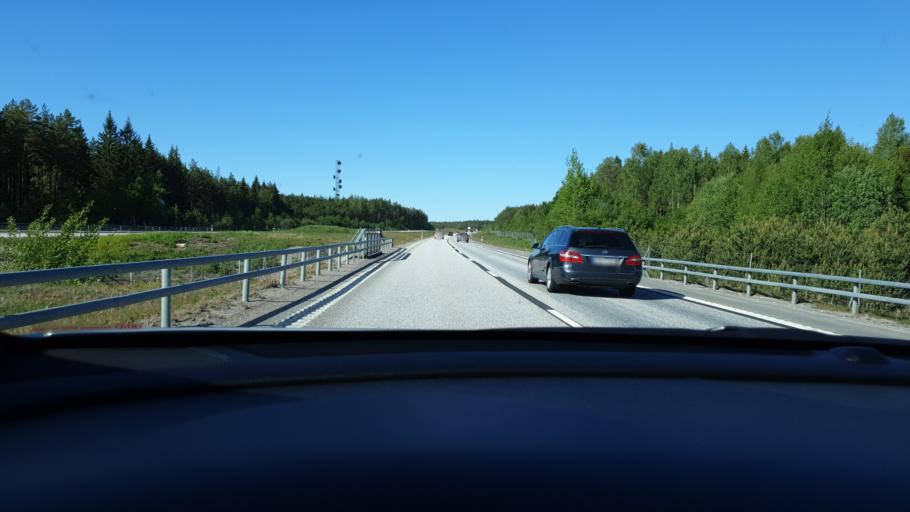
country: SE
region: Uppsala
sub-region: Tierps Kommun
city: Tierp
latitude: 60.2892
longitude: 17.5084
